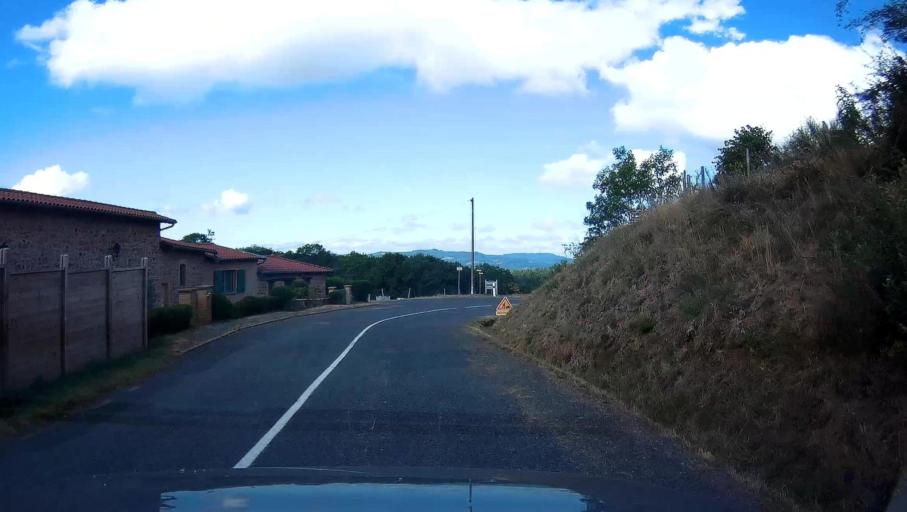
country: FR
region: Rhone-Alpes
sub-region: Departement du Rhone
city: Cogny
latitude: 45.9914
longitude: 4.5599
